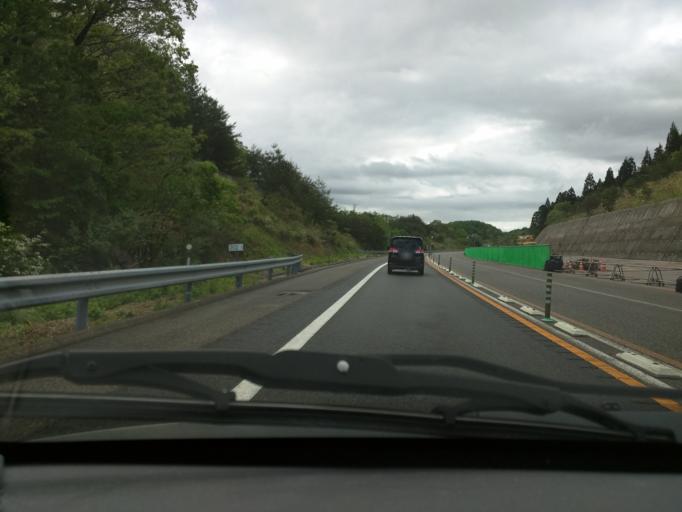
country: JP
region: Niigata
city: Joetsu
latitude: 37.1174
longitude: 138.2165
